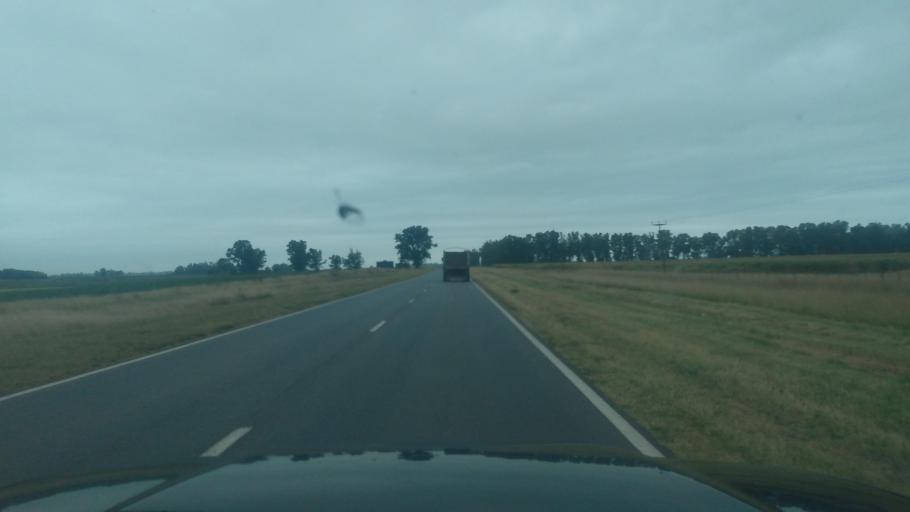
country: AR
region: Buenos Aires
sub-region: Partido de Nueve de Julio
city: Nueve de Julio
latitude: -35.4073
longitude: -60.7726
